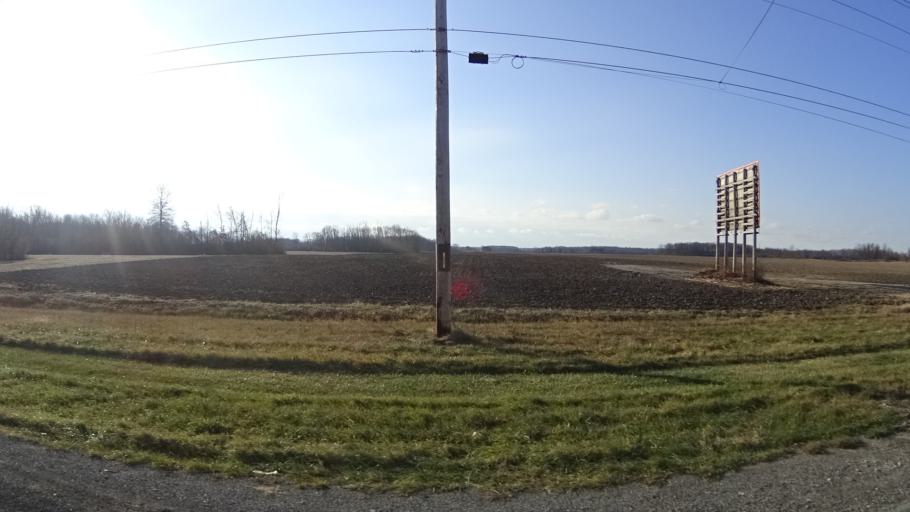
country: US
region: Ohio
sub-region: Lorain County
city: Oberlin
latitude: 41.2652
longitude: -82.2356
